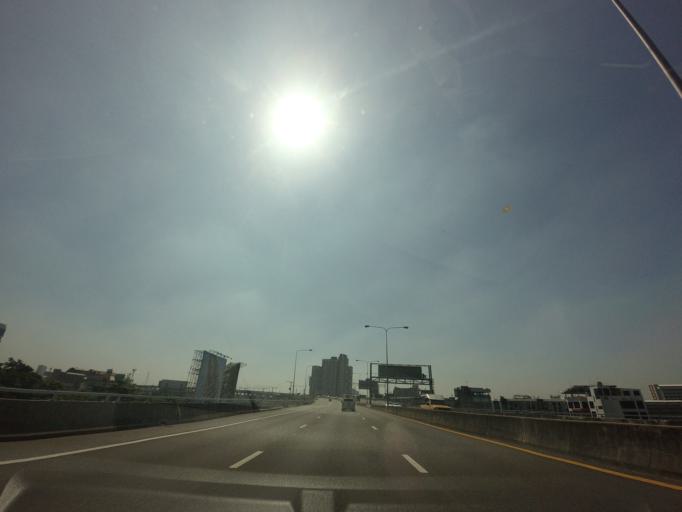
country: TH
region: Bangkok
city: Phra Khanong
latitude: 13.6780
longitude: 100.6037
